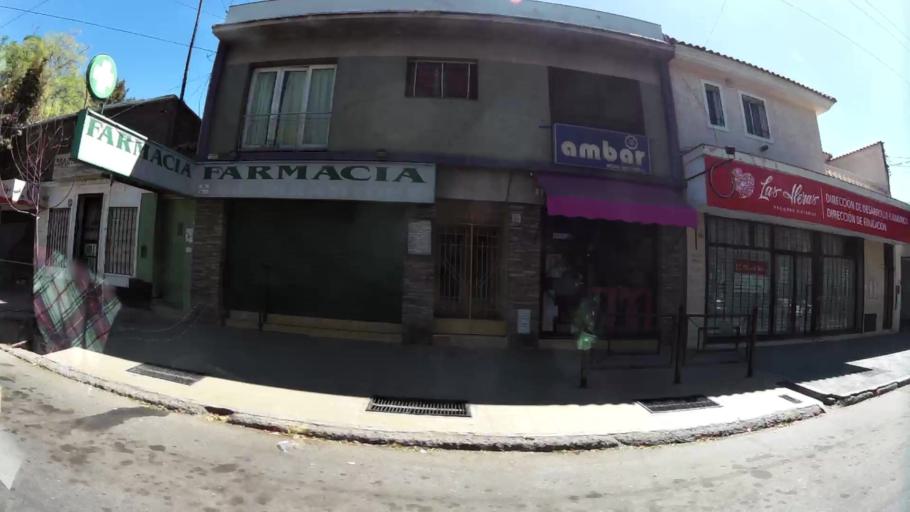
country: AR
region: Mendoza
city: Las Heras
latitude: -32.8515
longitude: -68.8414
